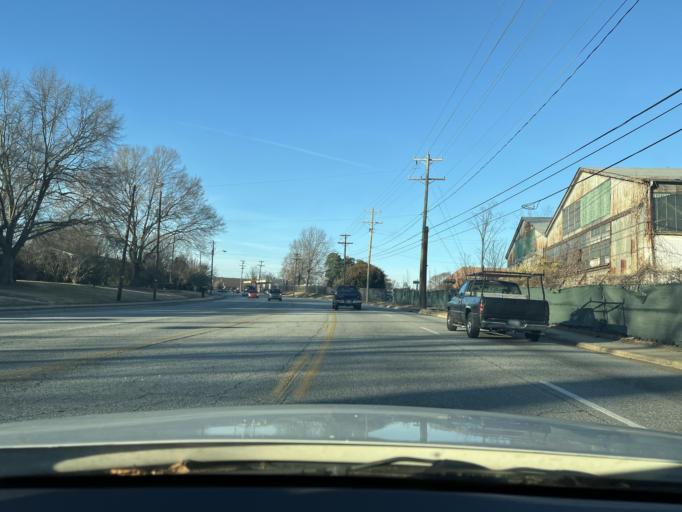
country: US
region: North Carolina
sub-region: Guilford County
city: Greensboro
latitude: 36.0516
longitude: -79.7915
